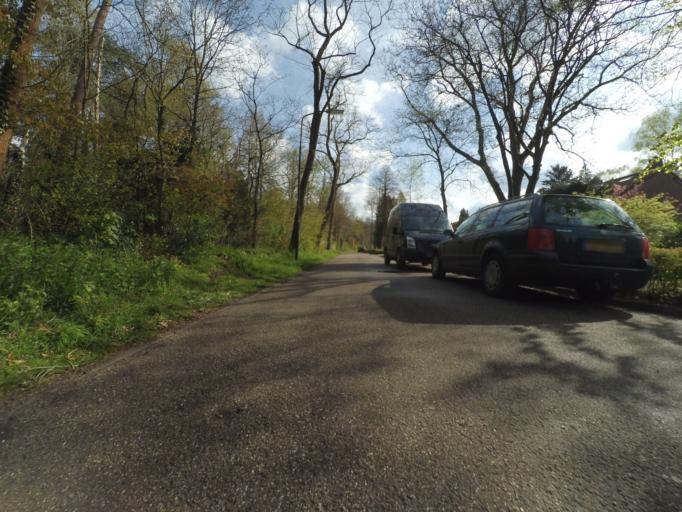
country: NL
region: Utrecht
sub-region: Gemeente Utrechtse Heuvelrug
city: Driebergen-Rijsenburg
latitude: 52.0603
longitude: 5.2999
